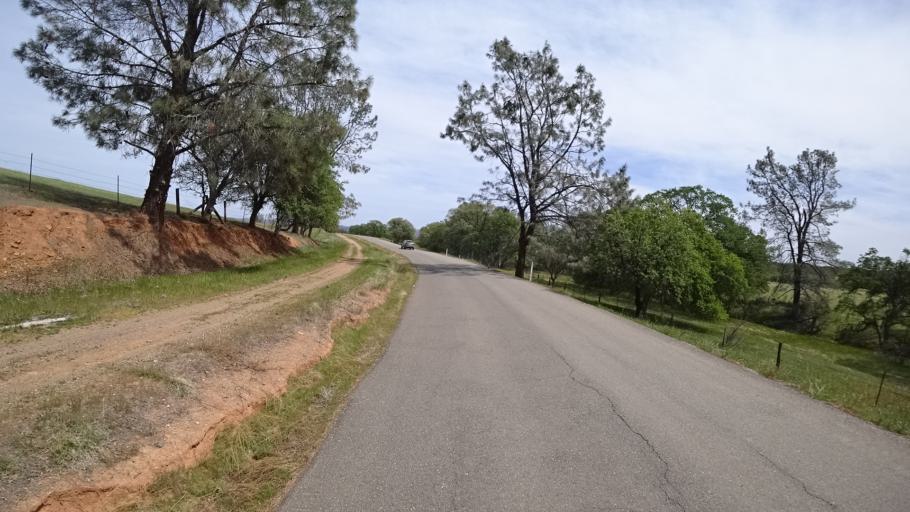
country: US
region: California
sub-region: Glenn County
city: Willows
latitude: 39.5763
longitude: -122.6035
